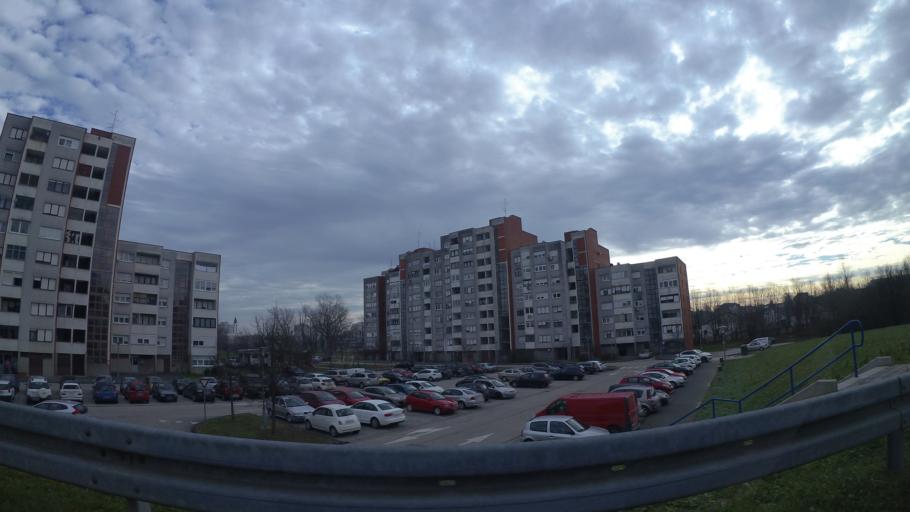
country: HR
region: Karlovacka
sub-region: Grad Karlovac
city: Karlovac
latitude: 45.4868
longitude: 15.5373
